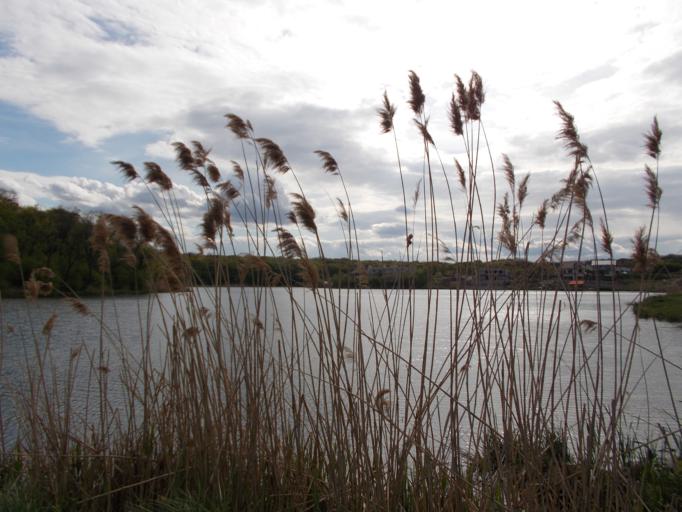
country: RO
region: Ilfov
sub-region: Comuna Branesti
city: Branesti
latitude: 44.4495
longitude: 26.3265
